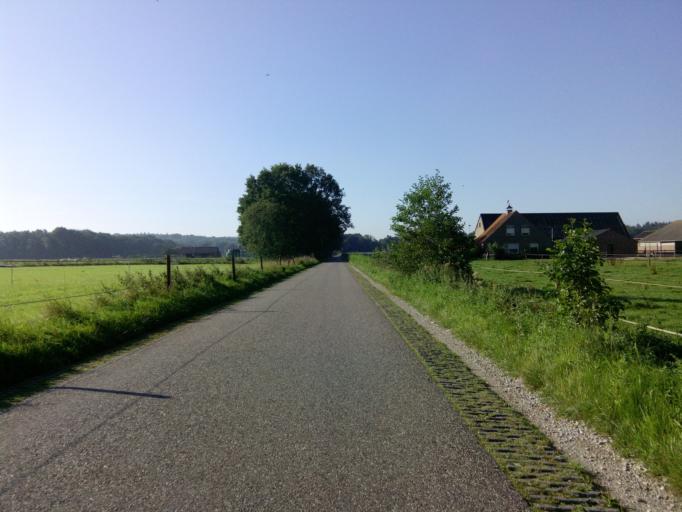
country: NL
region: Utrecht
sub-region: Gemeente Utrechtse Heuvelrug
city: Overberg
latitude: 52.0428
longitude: 5.4599
